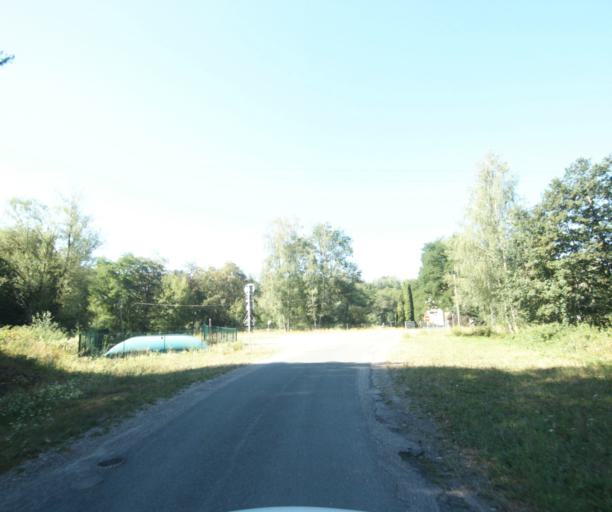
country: FR
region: Lorraine
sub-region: Departement des Vosges
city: Arches
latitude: 48.1480
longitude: 6.5005
